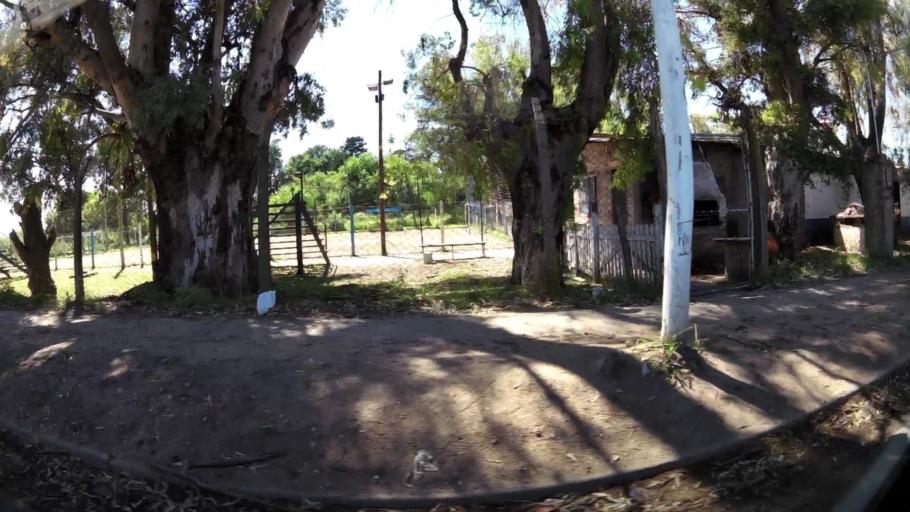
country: AR
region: Buenos Aires
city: Ituzaingo
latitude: -34.6724
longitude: -58.6615
